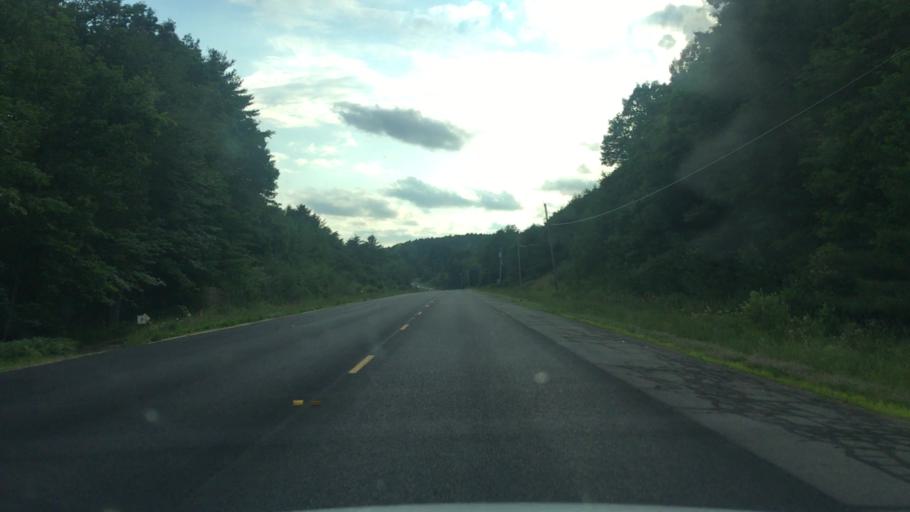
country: US
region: Maine
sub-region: Waldo County
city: Palermo
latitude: 44.3790
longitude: -69.4247
